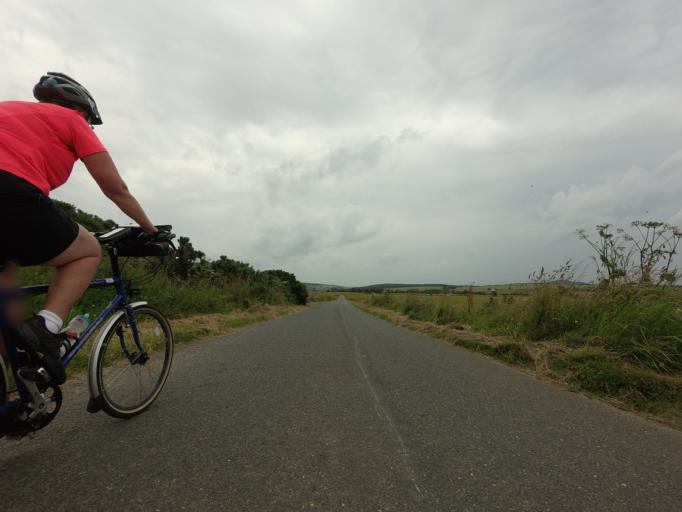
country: GB
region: Scotland
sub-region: Aberdeenshire
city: Portsoy
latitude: 57.6654
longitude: -2.7305
